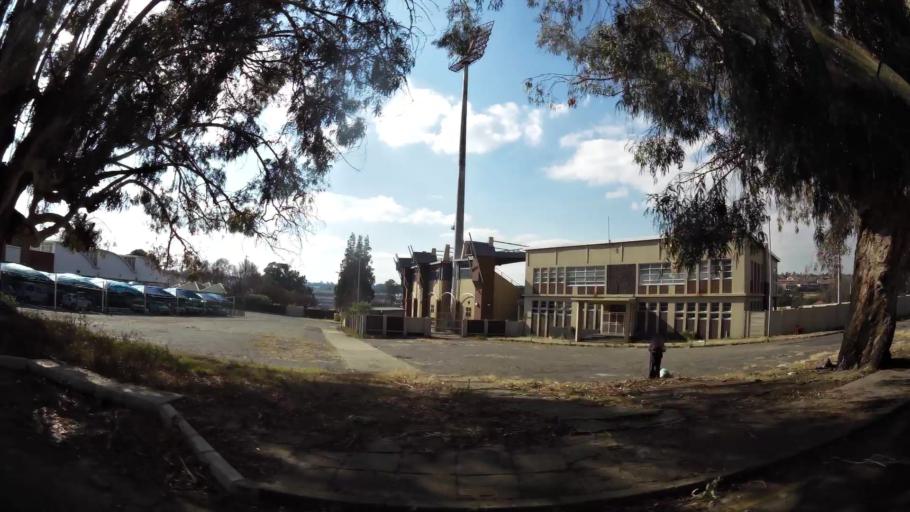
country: ZA
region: Gauteng
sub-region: West Rand District Municipality
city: Krugersdorp
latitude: -26.1030
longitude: 27.7767
